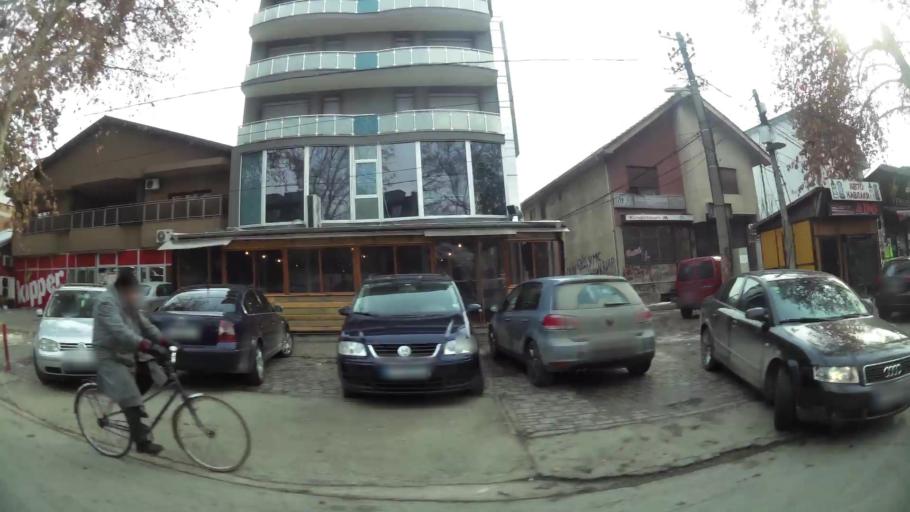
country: MK
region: Cair
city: Cair
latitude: 42.0125
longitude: 21.4453
